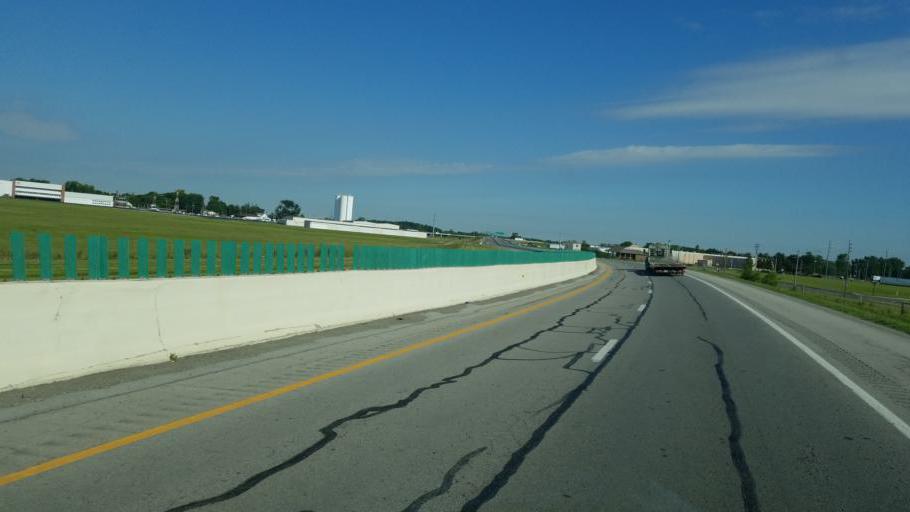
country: US
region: Ohio
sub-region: Hancock County
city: Findlay
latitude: 41.0197
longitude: -83.6615
